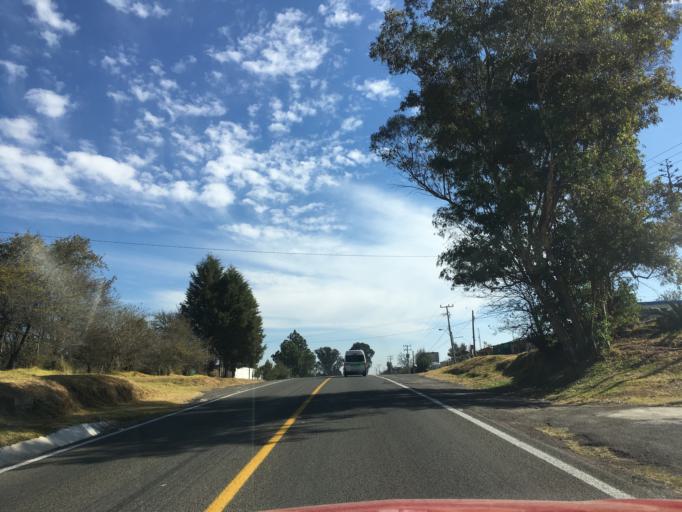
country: MX
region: Michoacan
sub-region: Hidalgo
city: San Lucas Huarirapeo (La Mesa de San Lucas)
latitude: 19.6661
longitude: -100.6777
